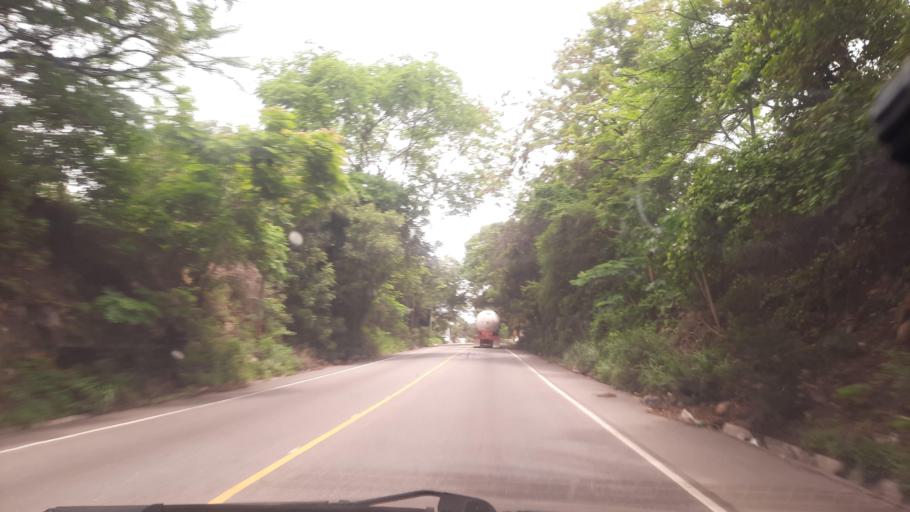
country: GT
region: Zacapa
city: Rio Hondo
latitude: 15.0708
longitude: -89.5108
